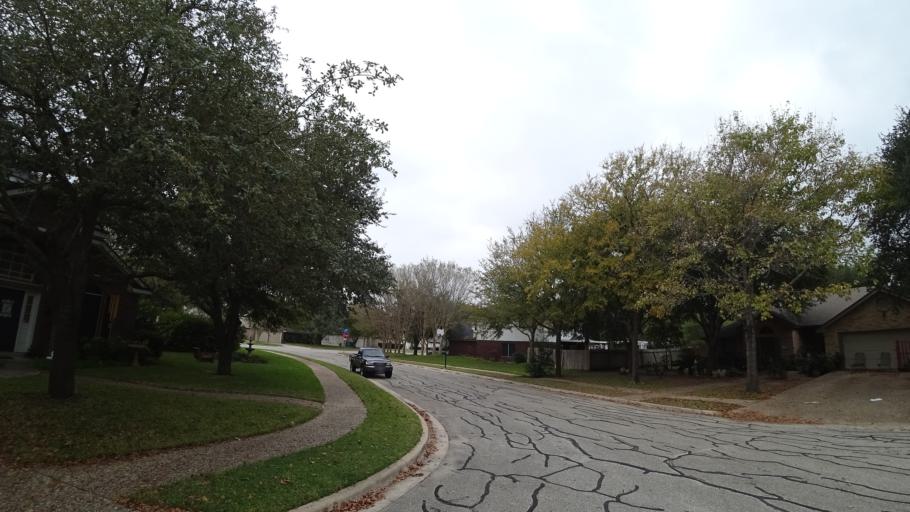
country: US
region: Texas
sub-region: Travis County
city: Pflugerville
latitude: 30.4465
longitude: -97.6101
